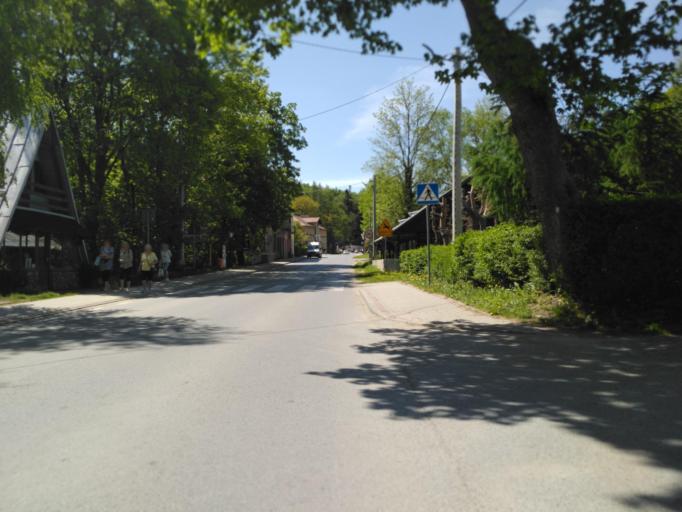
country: PL
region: Subcarpathian Voivodeship
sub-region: Powiat krosnienski
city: Iwonicz-Zdroj
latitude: 49.5673
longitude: 21.7932
